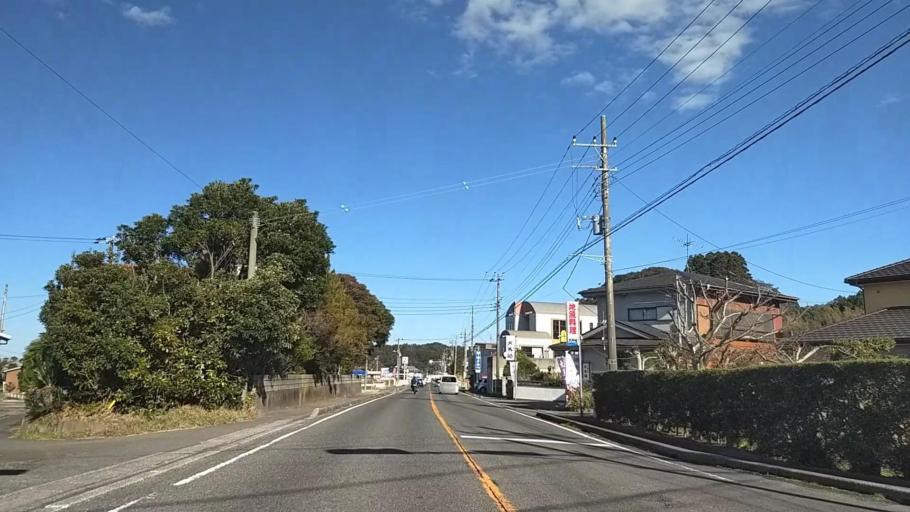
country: JP
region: Chiba
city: Ohara
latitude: 35.2193
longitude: 140.3796
